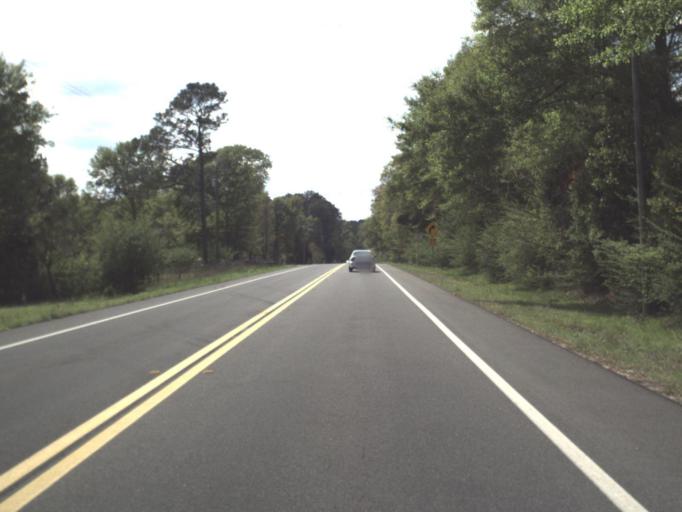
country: US
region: Alabama
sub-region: Covington County
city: Florala
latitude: 30.9634
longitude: -86.4362
